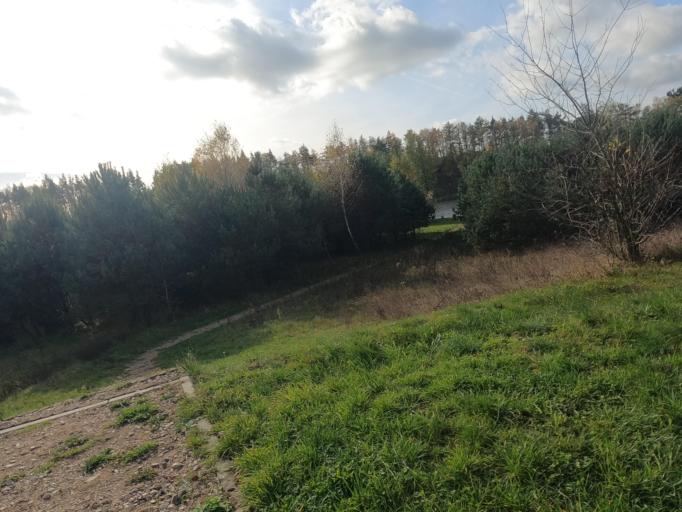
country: PL
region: Pomeranian Voivodeship
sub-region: Powiat starogardzki
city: Starogard Gdanski
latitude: 53.9723
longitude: 18.4812
